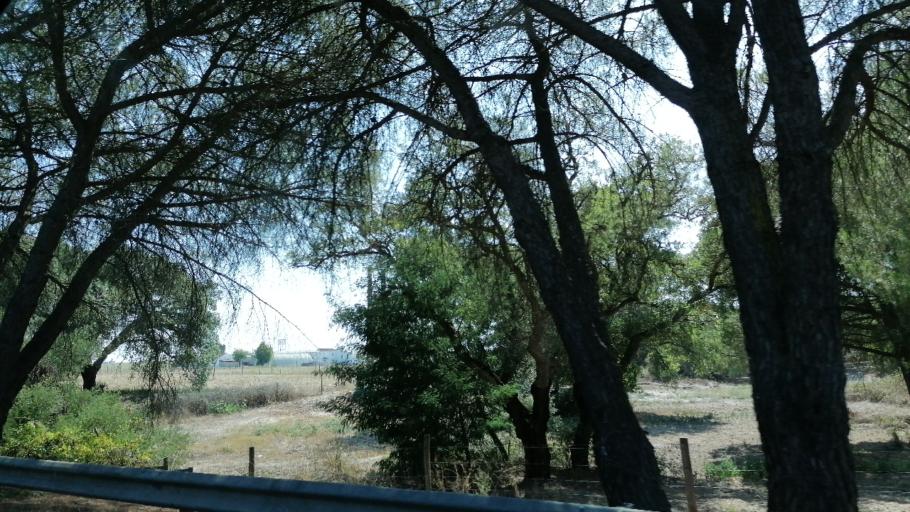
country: PT
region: Evora
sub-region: Vendas Novas
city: Vendas Novas
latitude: 38.7061
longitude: -8.6137
